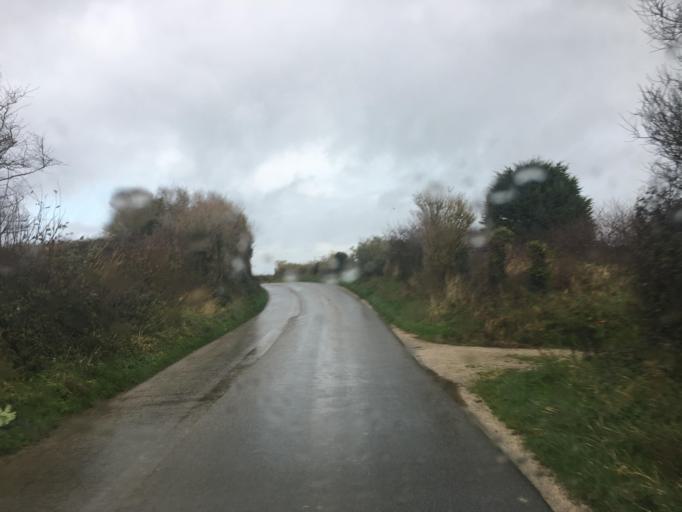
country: FR
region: Lower Normandy
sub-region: Departement de la Manche
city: Reville
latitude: 49.6906
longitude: -1.2780
